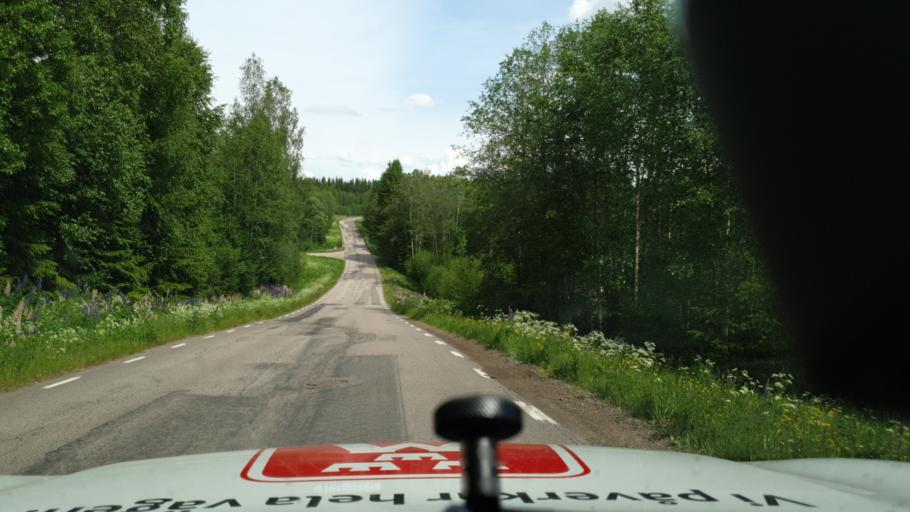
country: SE
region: Vaermland
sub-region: Torsby Kommun
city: Torsby
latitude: 59.9852
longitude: 12.8364
